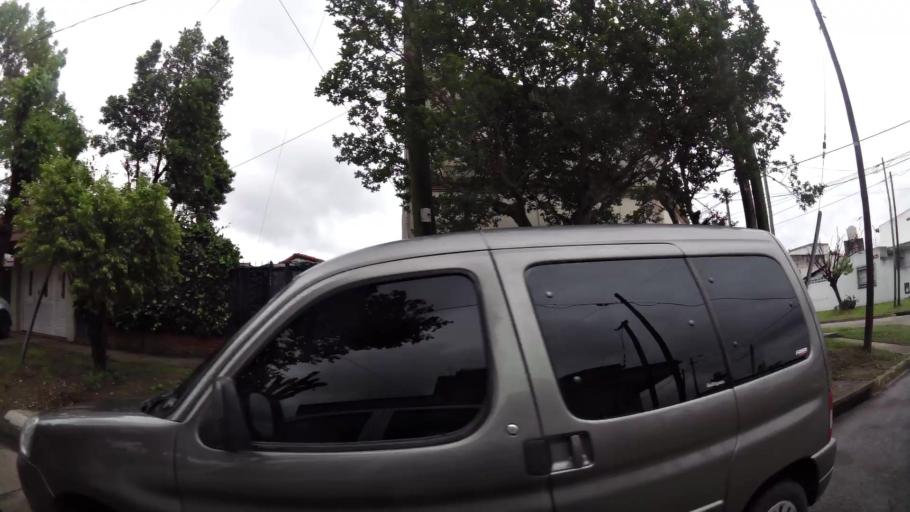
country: AR
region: Buenos Aires
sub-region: Partido de Lomas de Zamora
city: Lomas de Zamora
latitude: -34.7482
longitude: -58.3824
